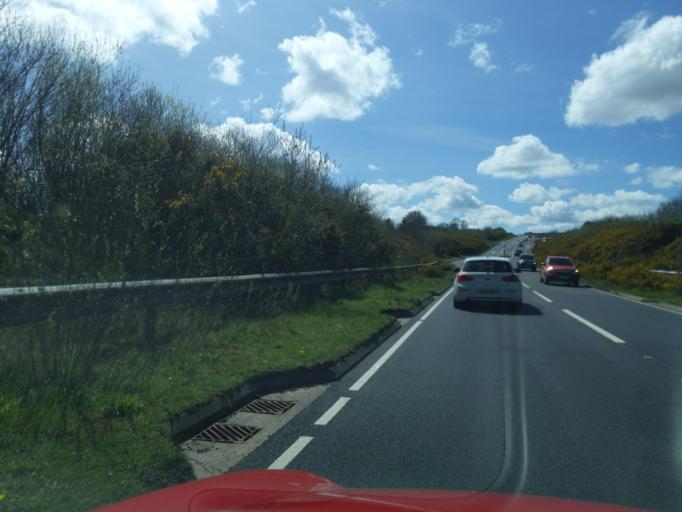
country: GB
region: England
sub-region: Cornwall
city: Liskeard
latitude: 50.4553
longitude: -4.5306
